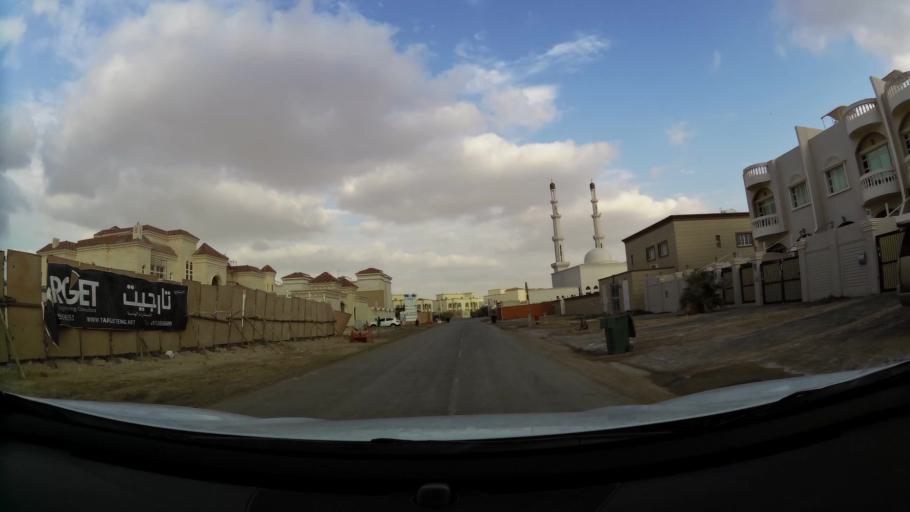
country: AE
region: Abu Dhabi
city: Abu Dhabi
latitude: 24.3669
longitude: 54.5511
